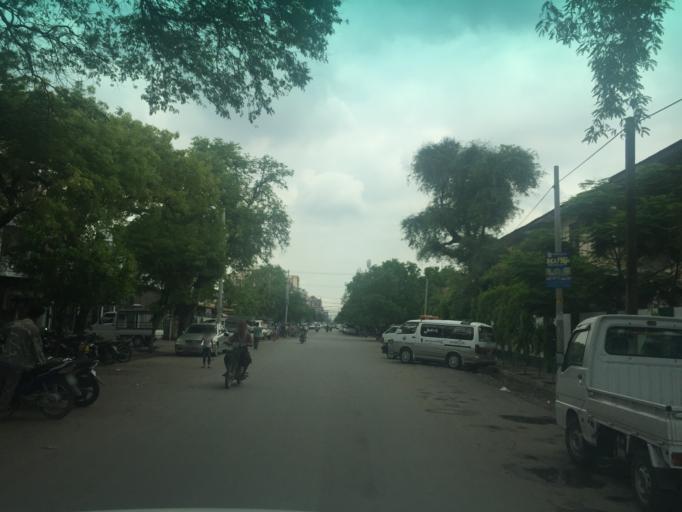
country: MM
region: Mandalay
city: Mandalay
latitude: 21.9672
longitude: 96.0786
